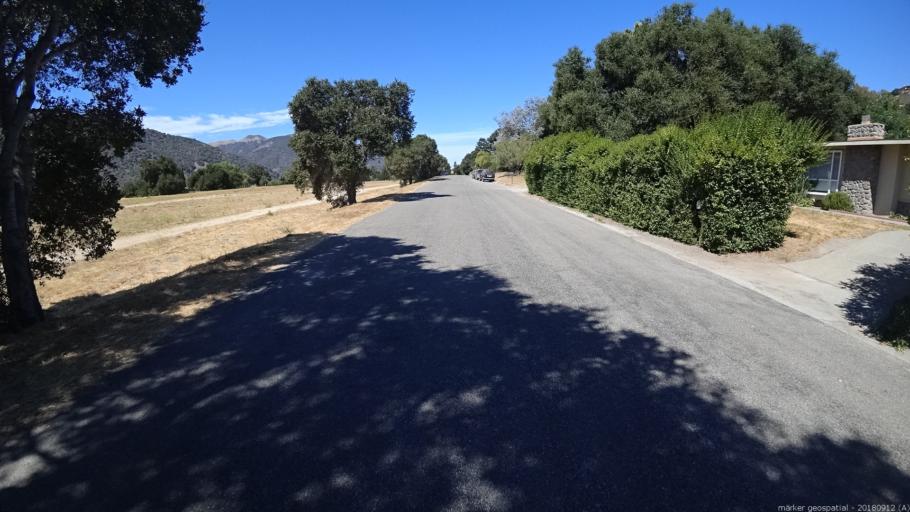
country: US
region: California
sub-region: Monterey County
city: Carmel Valley Village
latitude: 36.4831
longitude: -121.7309
